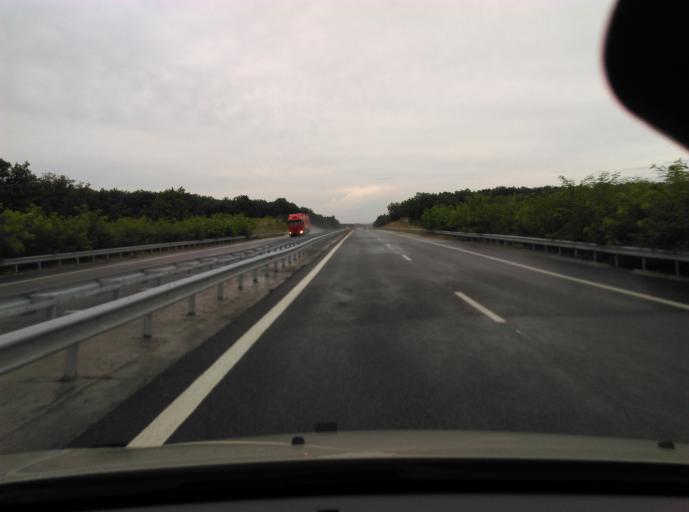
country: BG
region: Khaskovo
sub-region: Obshtina Dimitrovgrad
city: Dimitrovgrad
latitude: 42.0510
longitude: 25.4952
